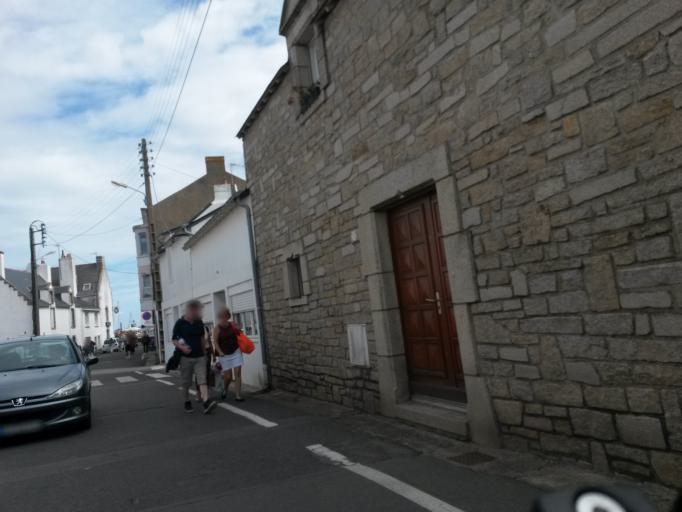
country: FR
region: Pays de la Loire
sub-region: Departement de la Loire-Atlantique
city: Le Croisic
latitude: 47.2919
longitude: -2.5105
